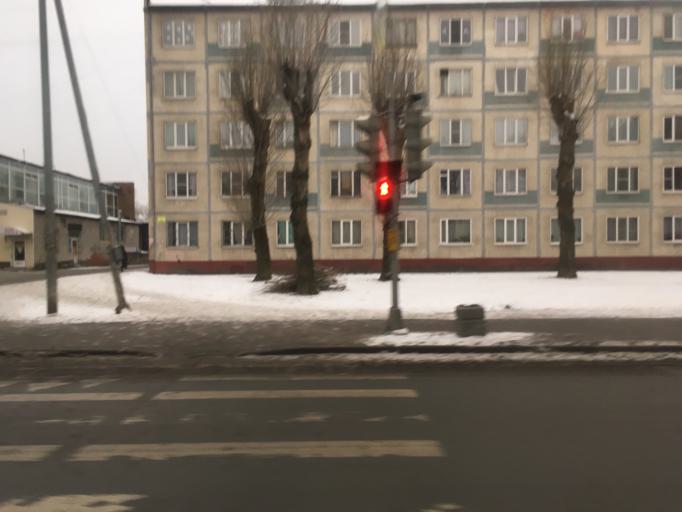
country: RU
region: St.-Petersburg
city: Obukhovo
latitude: 59.8658
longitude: 30.4440
